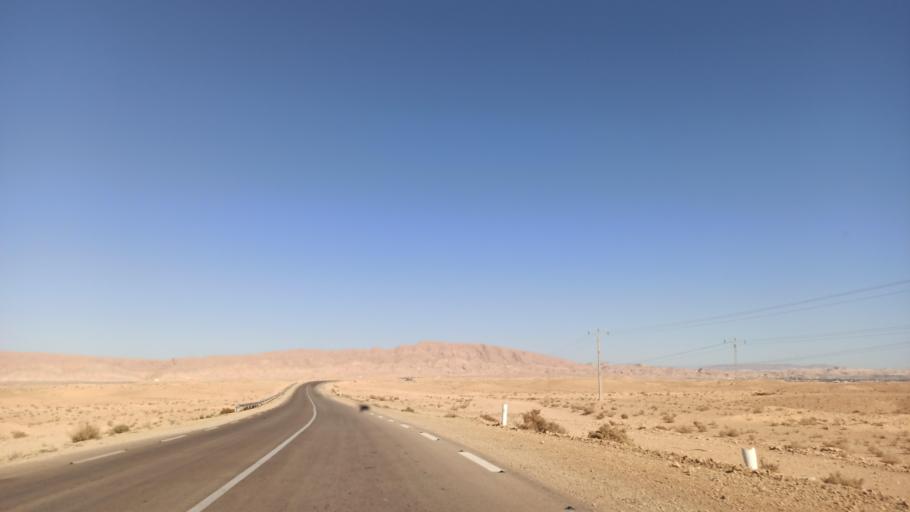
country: TN
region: Gafsa
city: Al Metlaoui
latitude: 34.2826
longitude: 8.3526
